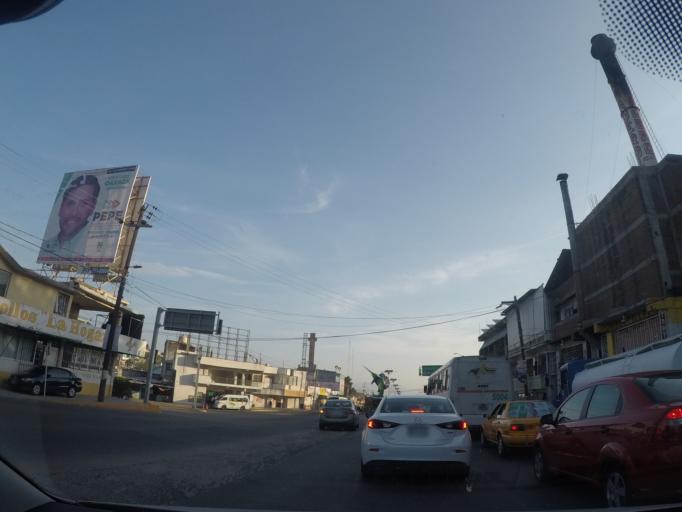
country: MX
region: Oaxaca
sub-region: Salina Cruz
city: Salina Cruz
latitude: 16.1960
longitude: -95.2017
